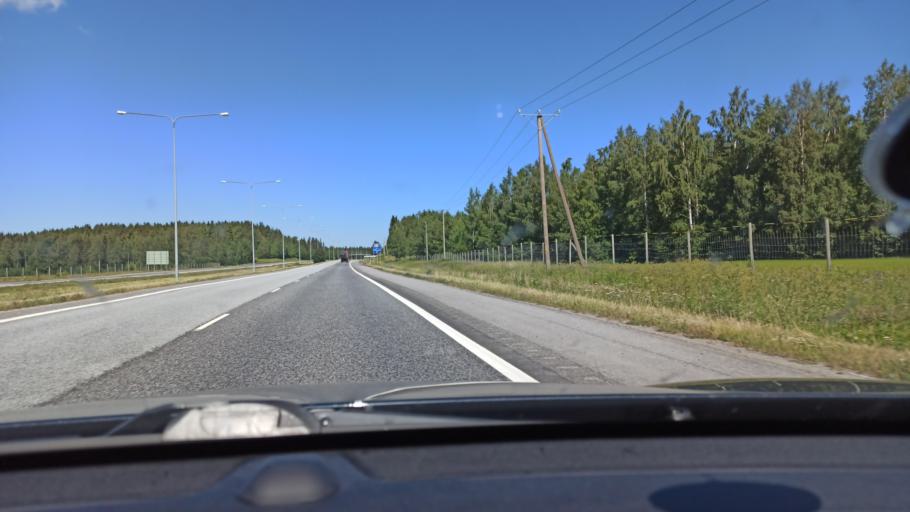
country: FI
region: Ostrobothnia
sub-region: Vaasa
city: Ristinummi
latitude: 63.0469
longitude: 21.7223
